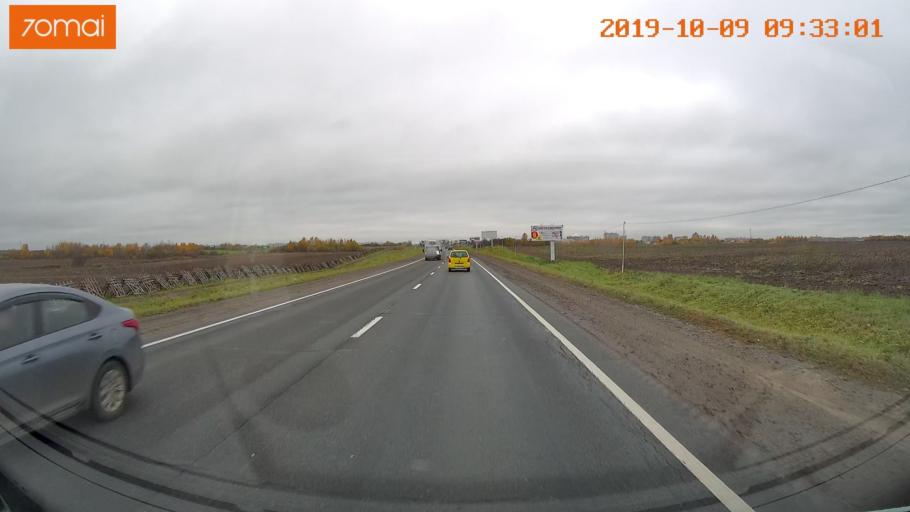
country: RU
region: Vologda
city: Vologda
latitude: 59.1645
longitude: 39.9210
